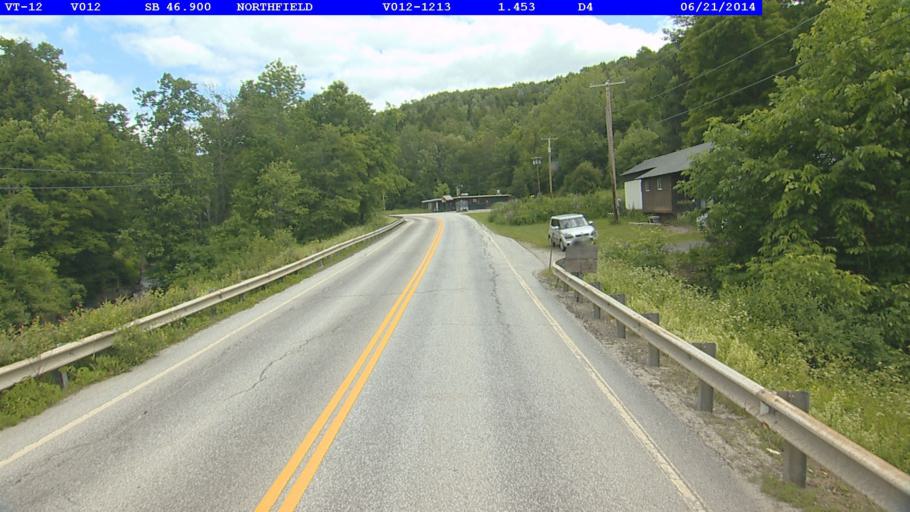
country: US
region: Vermont
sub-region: Washington County
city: Northfield
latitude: 44.1112
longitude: -72.6505
